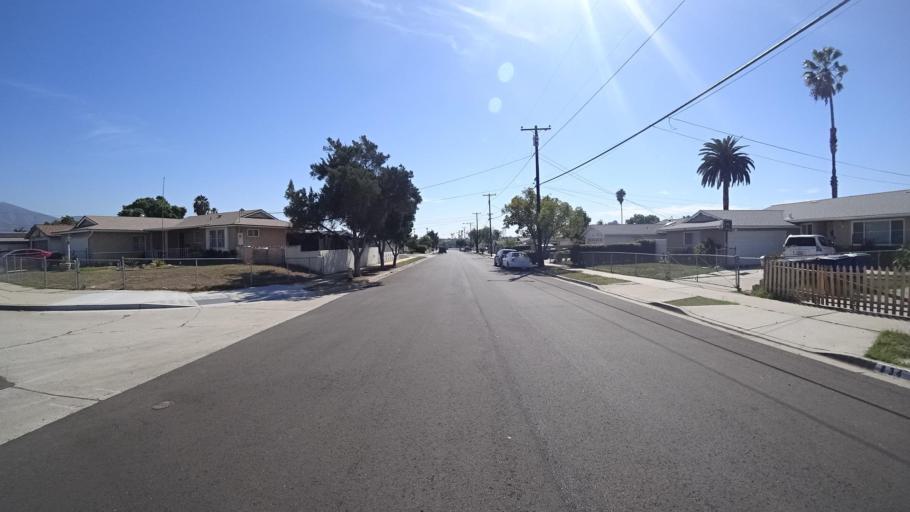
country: US
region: California
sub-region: San Diego County
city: La Presa
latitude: 32.7114
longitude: -117.0116
